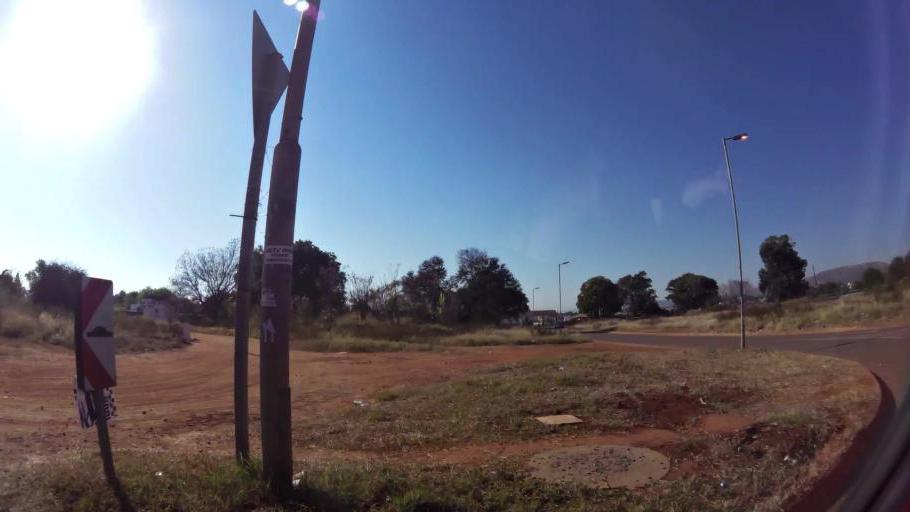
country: ZA
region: Gauteng
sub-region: City of Tshwane Metropolitan Municipality
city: Pretoria
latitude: -25.6567
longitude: 28.1435
